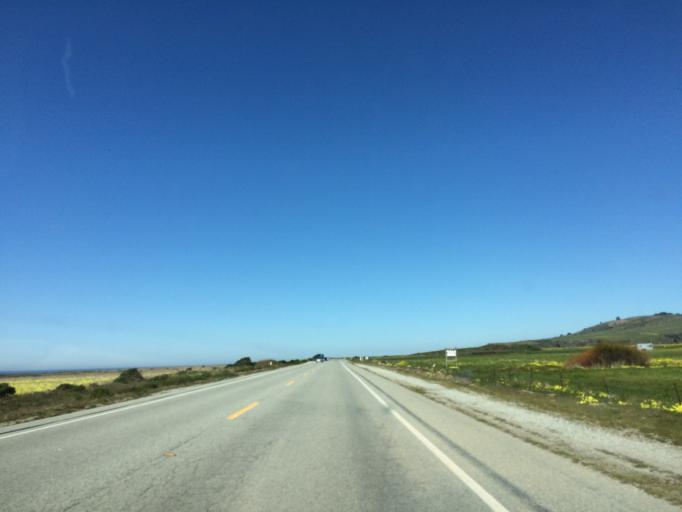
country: US
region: California
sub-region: Santa Cruz County
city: Bonny Doon
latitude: 37.0312
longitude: -122.2202
